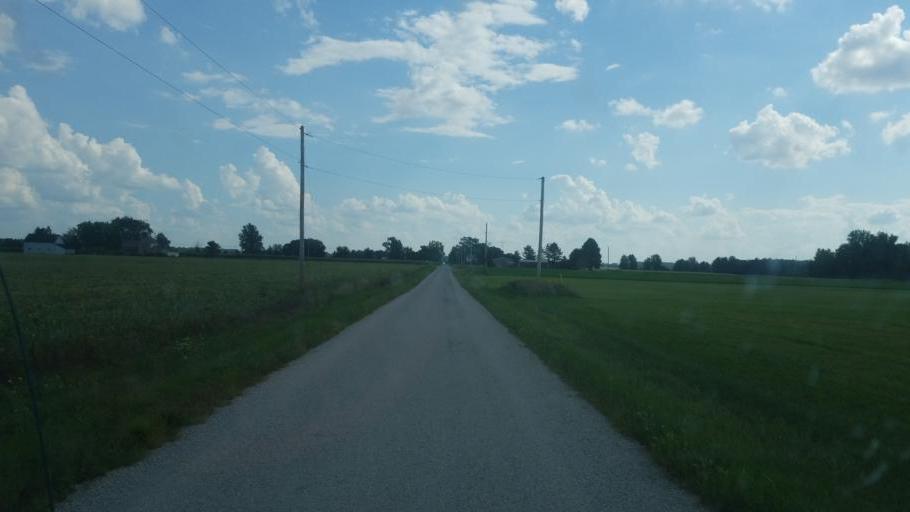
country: US
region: Ohio
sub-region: Huron County
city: Willard
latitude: 40.9845
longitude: -82.8160
